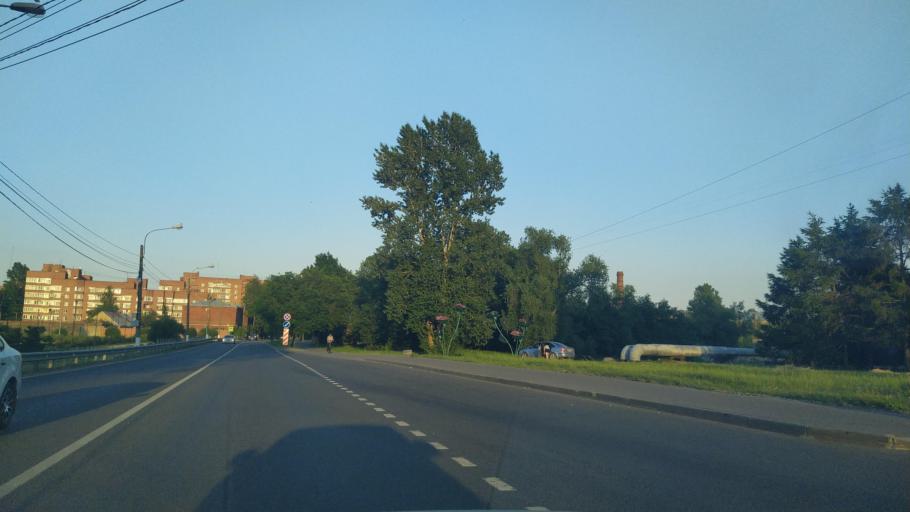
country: RU
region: St.-Petersburg
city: Kronshtadt
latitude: 60.0025
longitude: 29.7582
